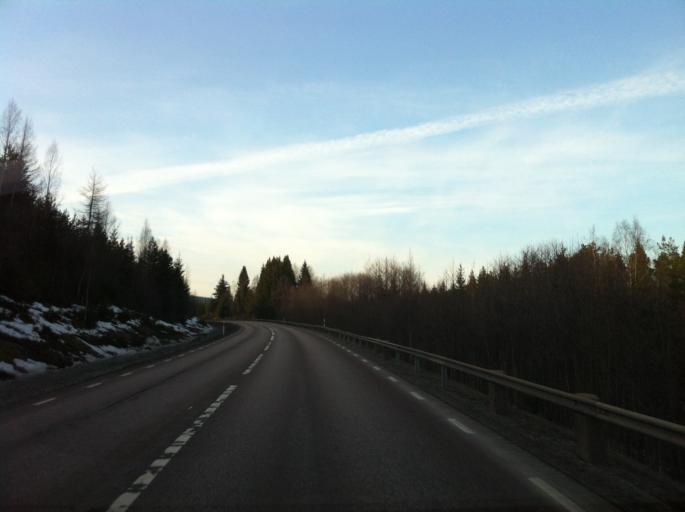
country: SE
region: Vaermland
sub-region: Filipstads Kommun
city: Lesjofors
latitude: 59.8780
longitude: 14.2685
